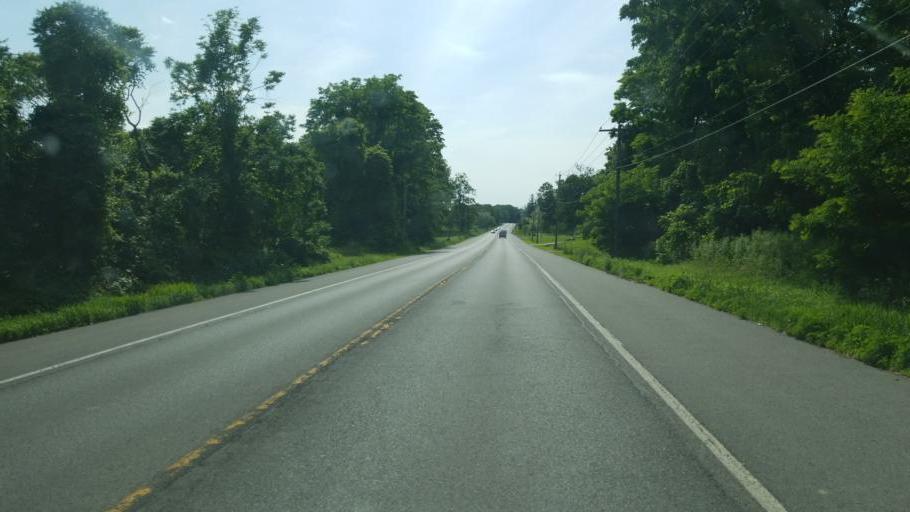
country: US
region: New York
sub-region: Ontario County
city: Holcomb
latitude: 42.9034
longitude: -77.5042
